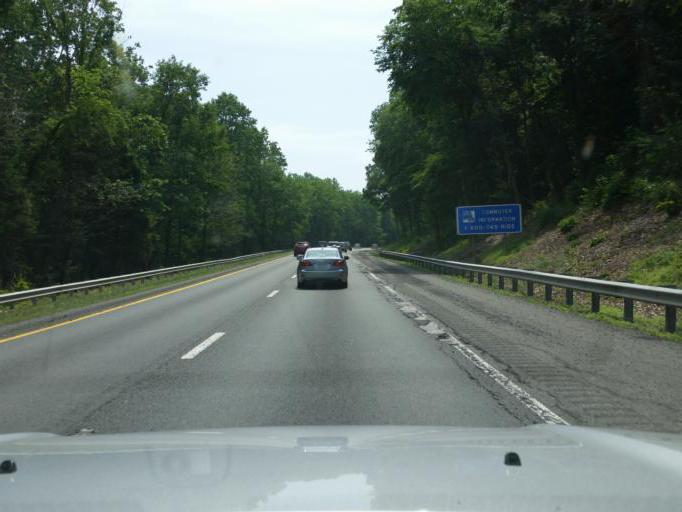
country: US
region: Maryland
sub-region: Frederick County
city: Green Valley
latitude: 39.2731
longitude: -77.3180
